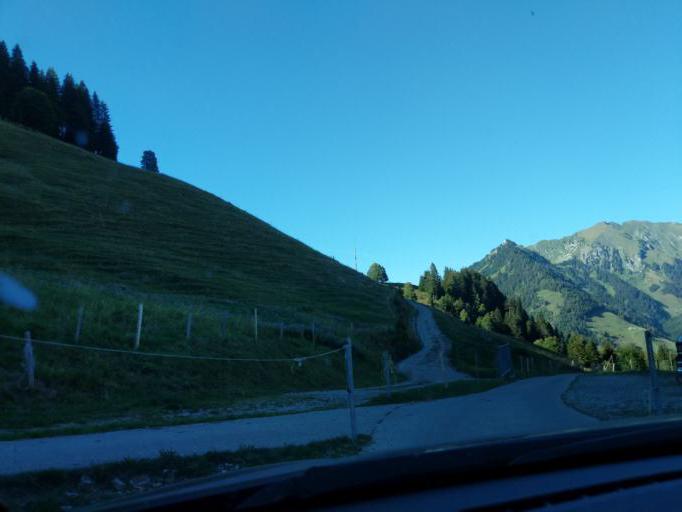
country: CH
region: Fribourg
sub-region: Gruyere District
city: Charmey
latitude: 46.5967
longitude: 7.2673
